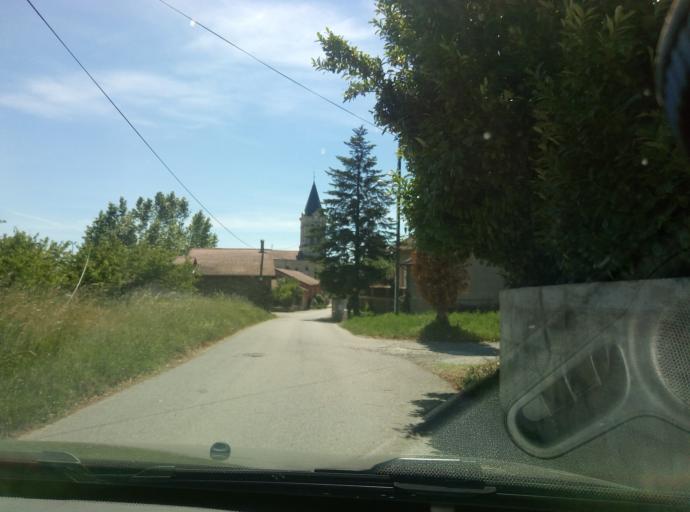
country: FR
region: Rhone-Alpes
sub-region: Departement de la Drome
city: Chanos-Curson
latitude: 45.0624
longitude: 4.9152
